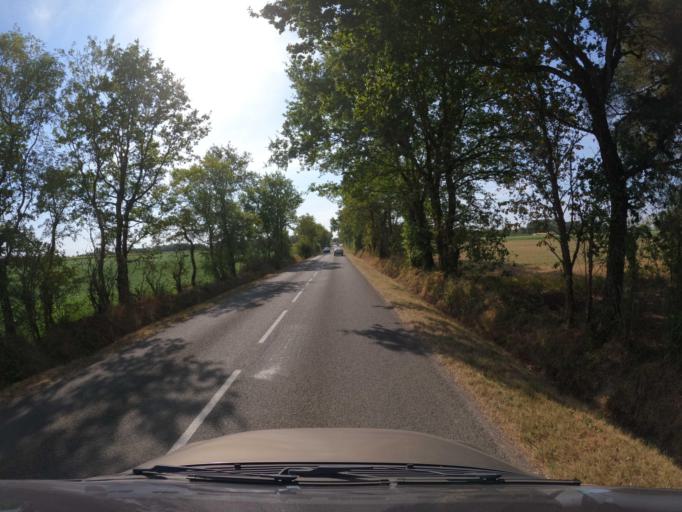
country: FR
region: Pays de la Loire
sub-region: Departement de la Vendee
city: Saint-Christophe-du-Ligneron
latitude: 46.8017
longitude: -1.7949
